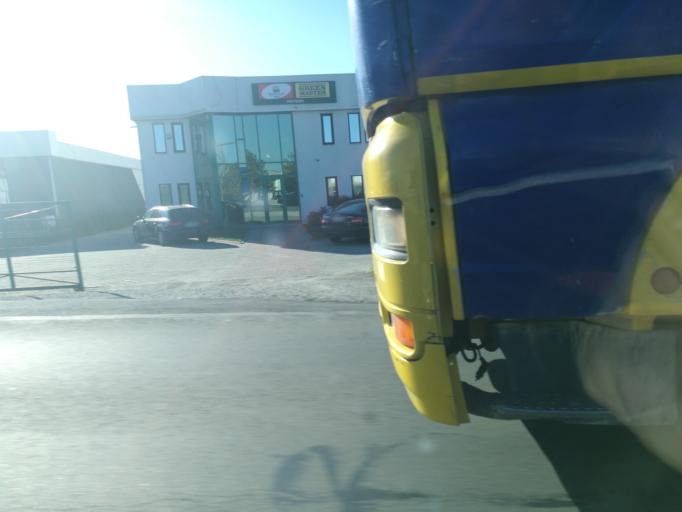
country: RO
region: Brasov
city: Brasov
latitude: 45.6871
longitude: 25.5827
